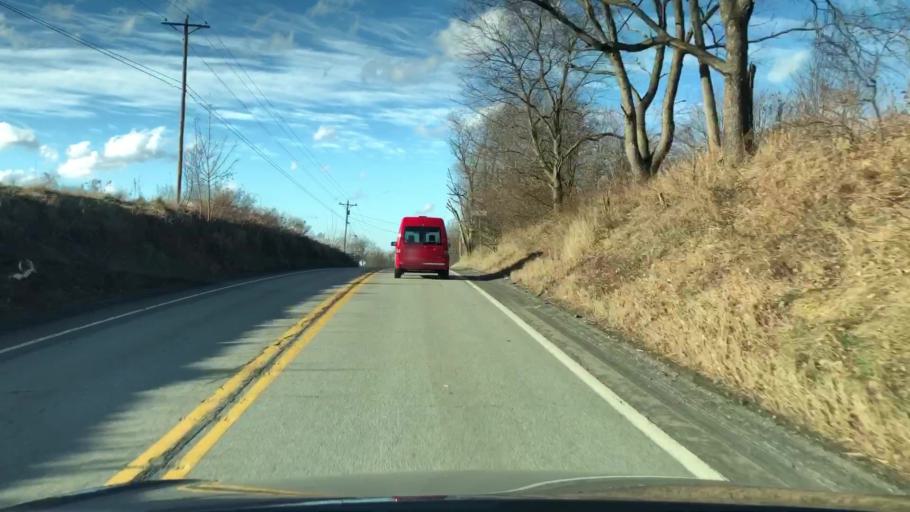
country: US
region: Pennsylvania
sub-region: Butler County
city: Meadowood
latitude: 40.8144
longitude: -79.8452
